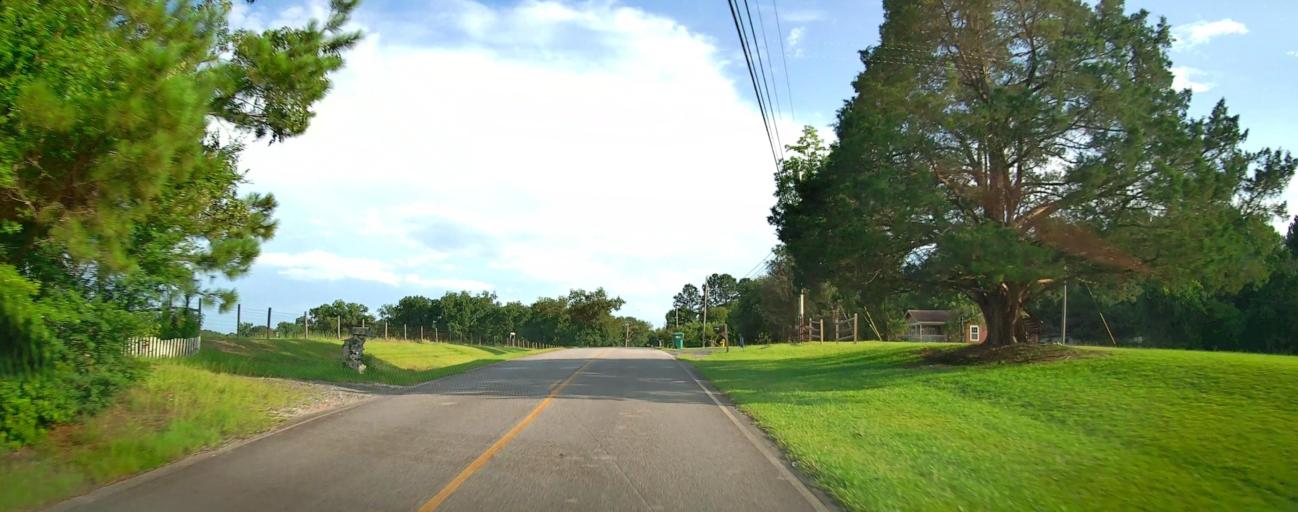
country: US
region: Georgia
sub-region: Peach County
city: Byron
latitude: 32.7211
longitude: -83.7468
